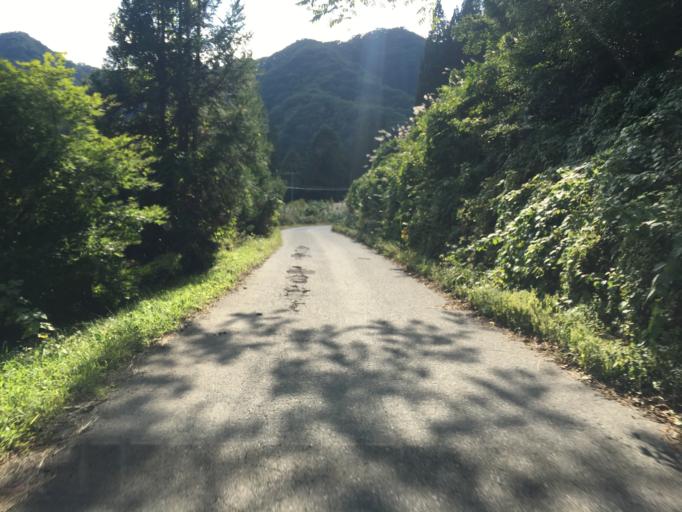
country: JP
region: Yamagata
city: Yonezawa
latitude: 37.8481
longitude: 140.1829
